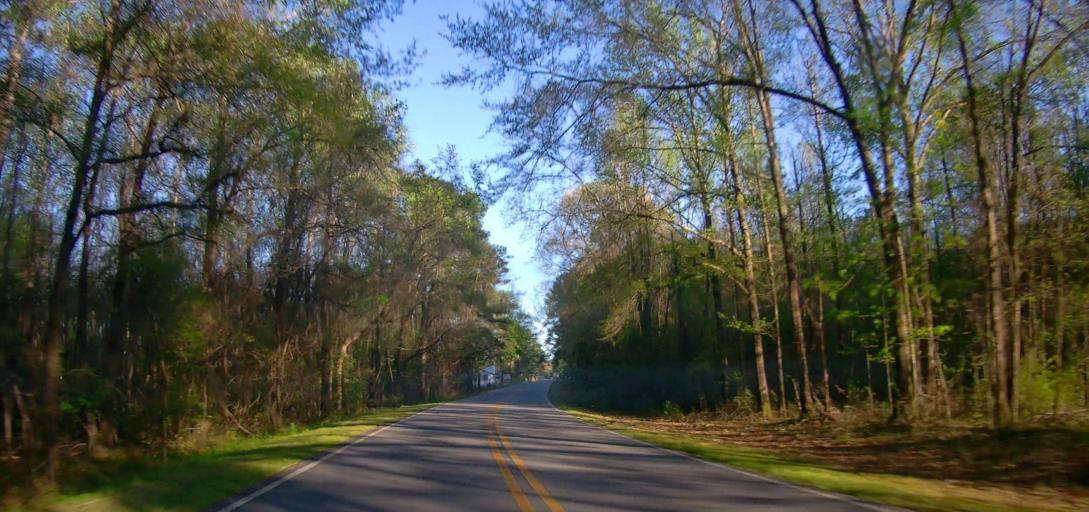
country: US
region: Georgia
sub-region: Wilkinson County
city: Irwinton
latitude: 32.8538
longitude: -83.2201
